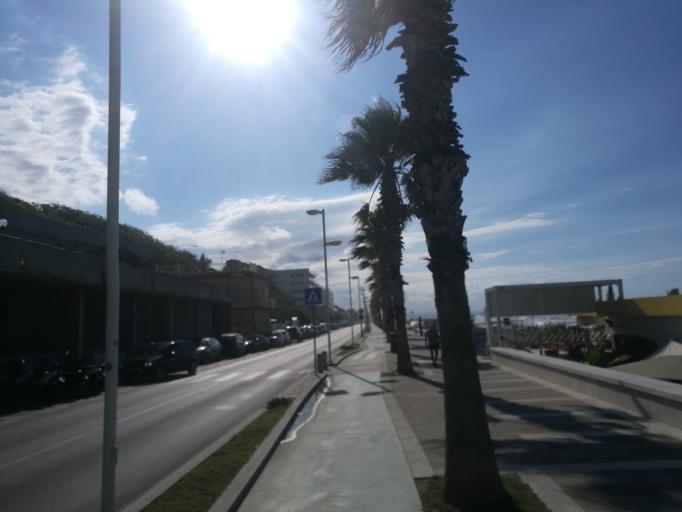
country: IT
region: Molise
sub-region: Provincia di Campobasso
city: Termoli
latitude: 42.0055
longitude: 14.9856
